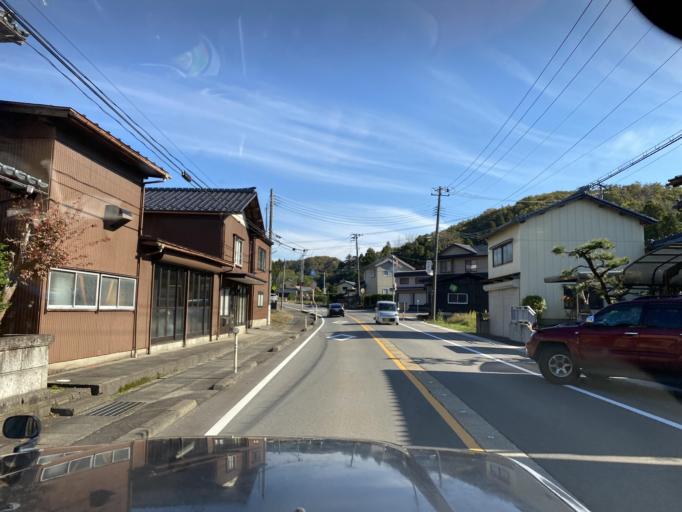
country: JP
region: Niigata
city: Niitsu-honcho
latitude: 37.7509
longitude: 139.0995
